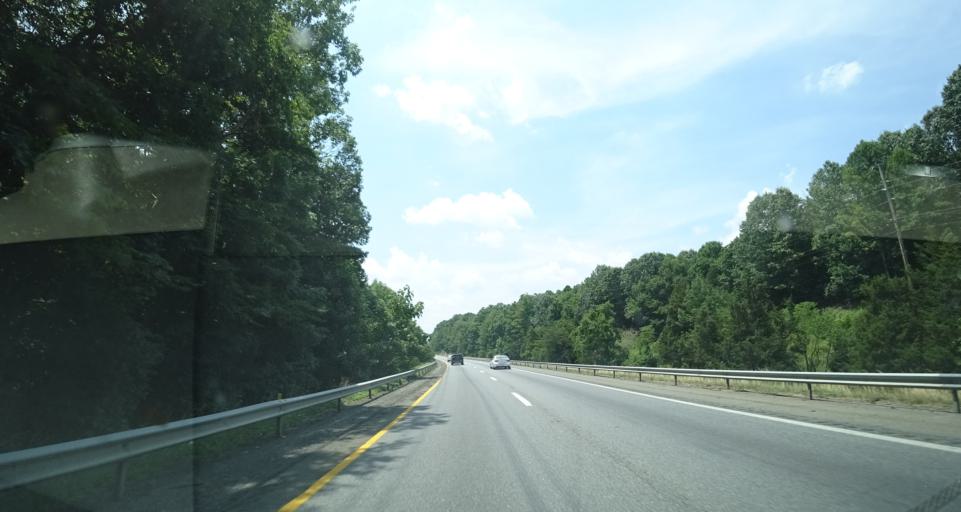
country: US
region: Virginia
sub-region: City of Radford
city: Radford
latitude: 37.1004
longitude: -80.5563
